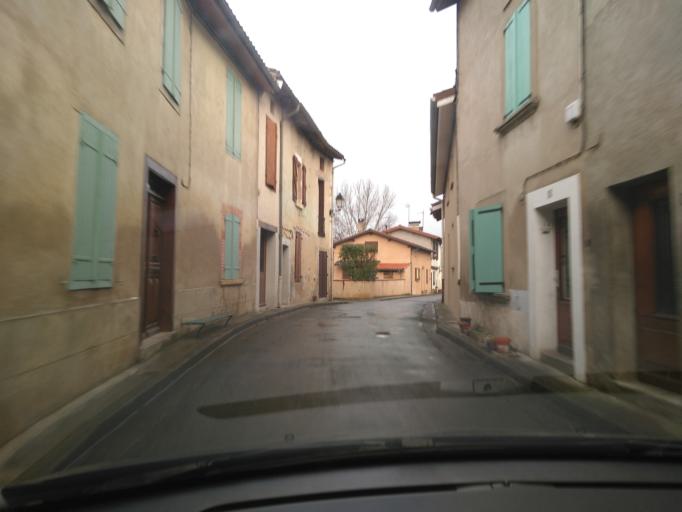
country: FR
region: Midi-Pyrenees
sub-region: Departement de la Haute-Garonne
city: Montesquieu-Volvestre
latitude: 43.1417
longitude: 1.3092
